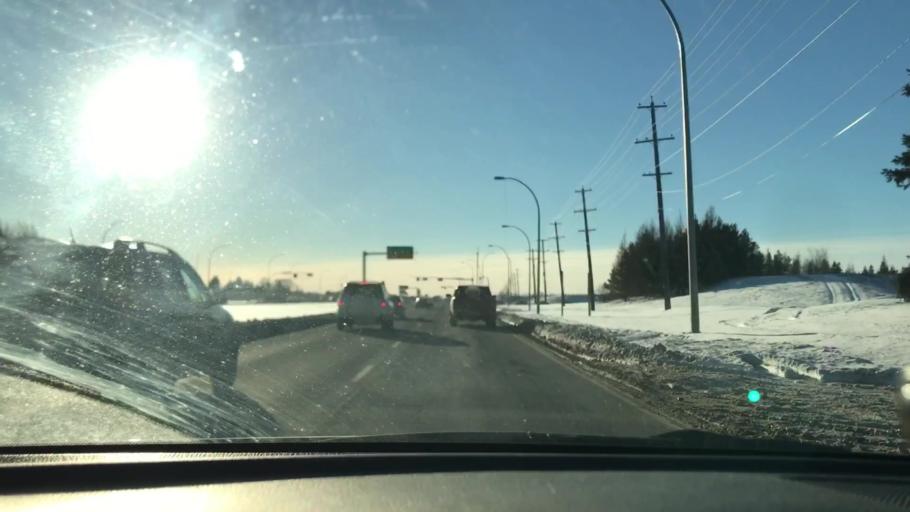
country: CA
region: Alberta
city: Edmonton
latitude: 53.4852
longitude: -113.4673
